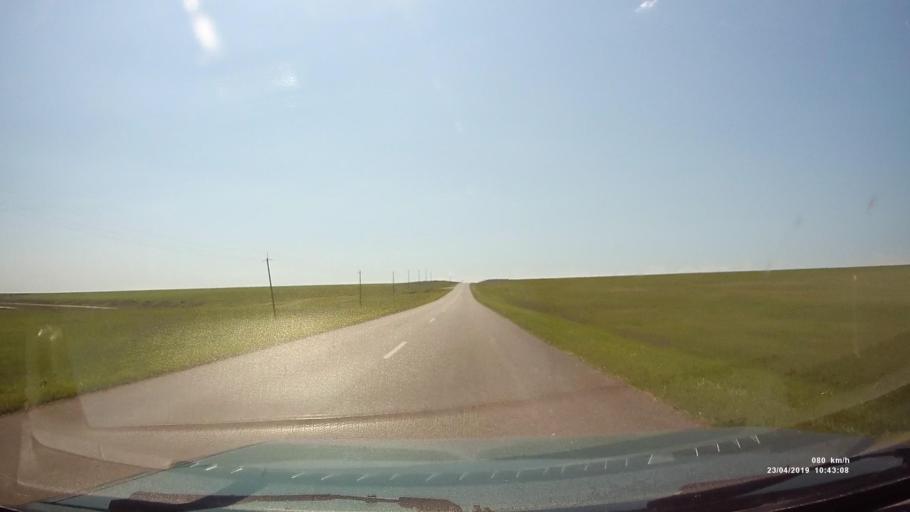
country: RU
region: Kalmykiya
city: Yashalta
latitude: 46.4738
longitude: 42.6486
